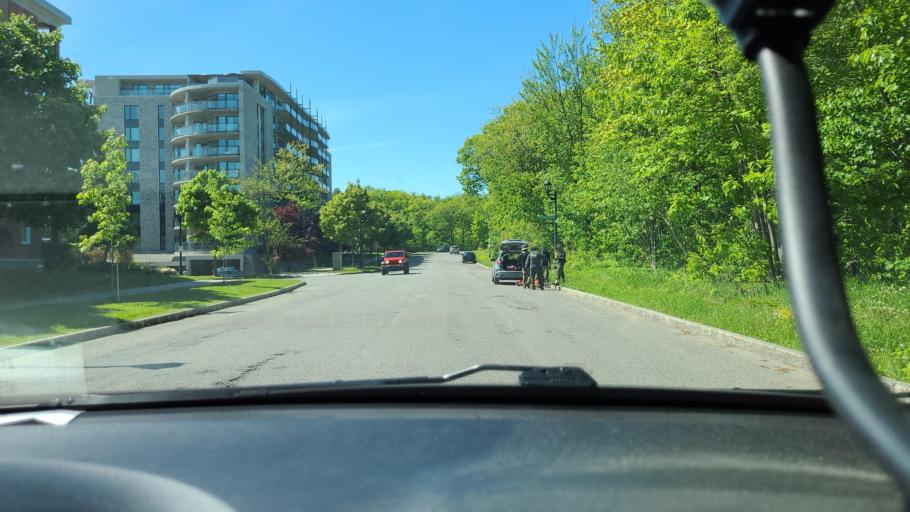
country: CA
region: Quebec
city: L'Ancienne-Lorette
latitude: 46.7554
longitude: -71.3253
